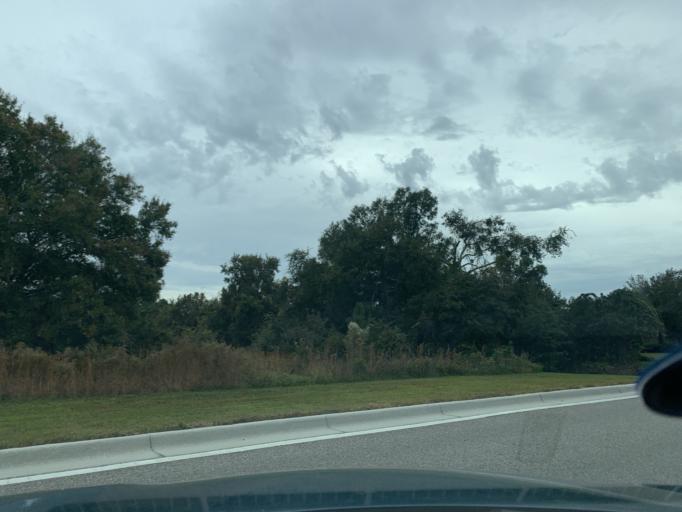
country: US
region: Florida
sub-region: Pasco County
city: Land O' Lakes
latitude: 28.3026
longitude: -82.4987
